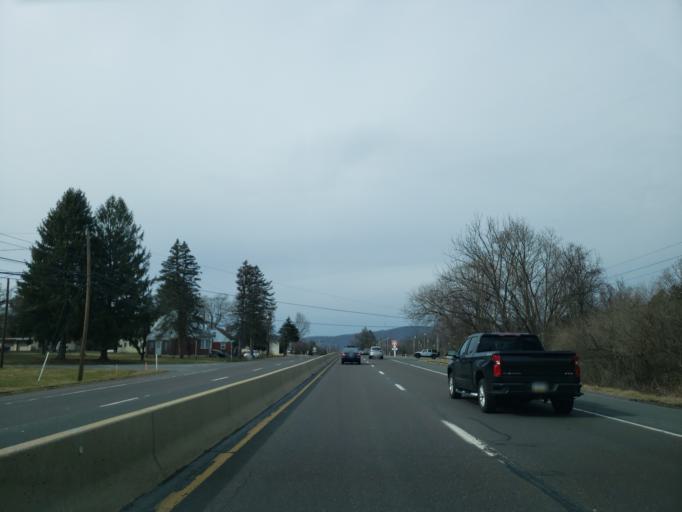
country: US
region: Pennsylvania
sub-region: Lehigh County
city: Coopersburg
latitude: 40.5358
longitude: -75.4081
